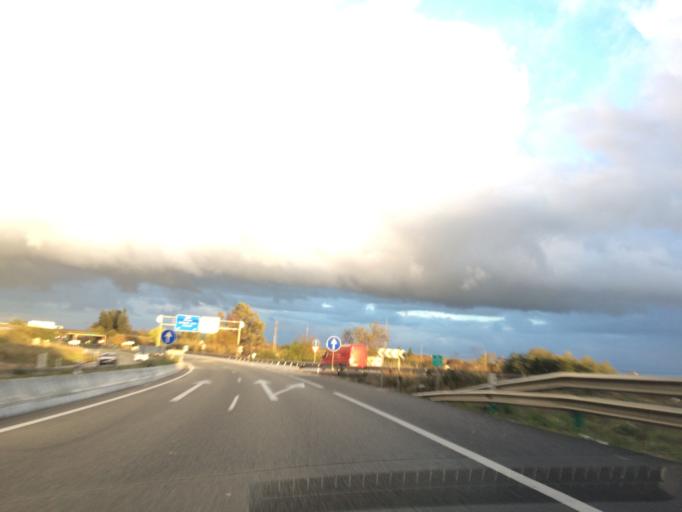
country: ES
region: Andalusia
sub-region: Provincia de Sevilla
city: Alcala de Guadaira
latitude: 37.3285
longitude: -5.8184
